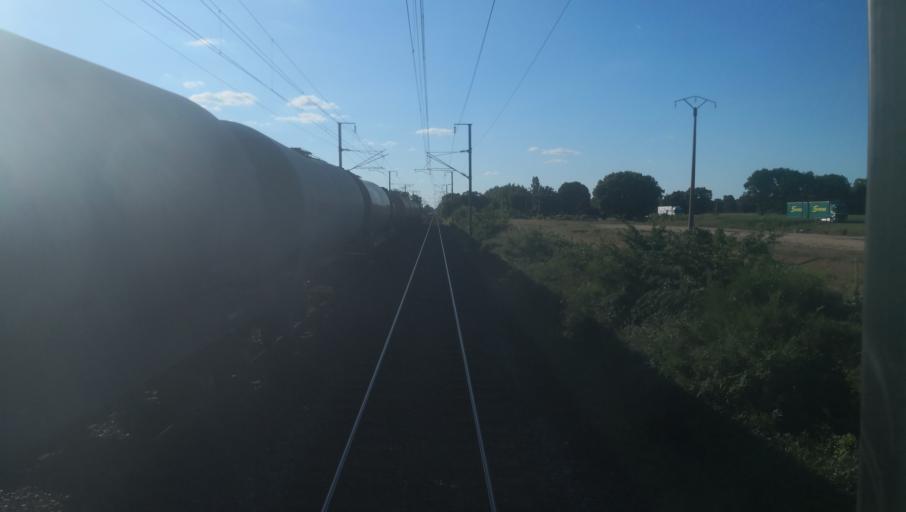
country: FR
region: Bourgogne
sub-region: Departement de la Nievre
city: Chantenay-Saint-Imbert
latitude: 46.6811
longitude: 3.2255
